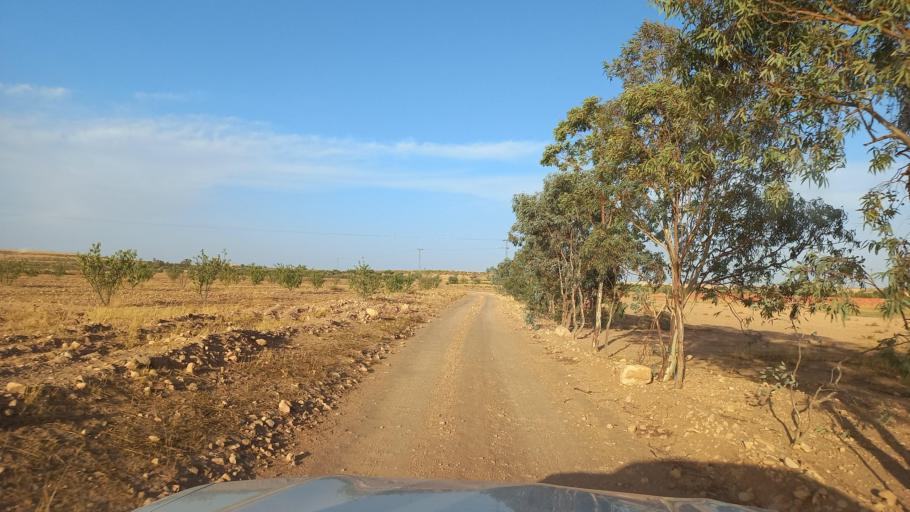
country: TN
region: Al Qasrayn
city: Kasserine
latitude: 35.2566
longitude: 8.9120
